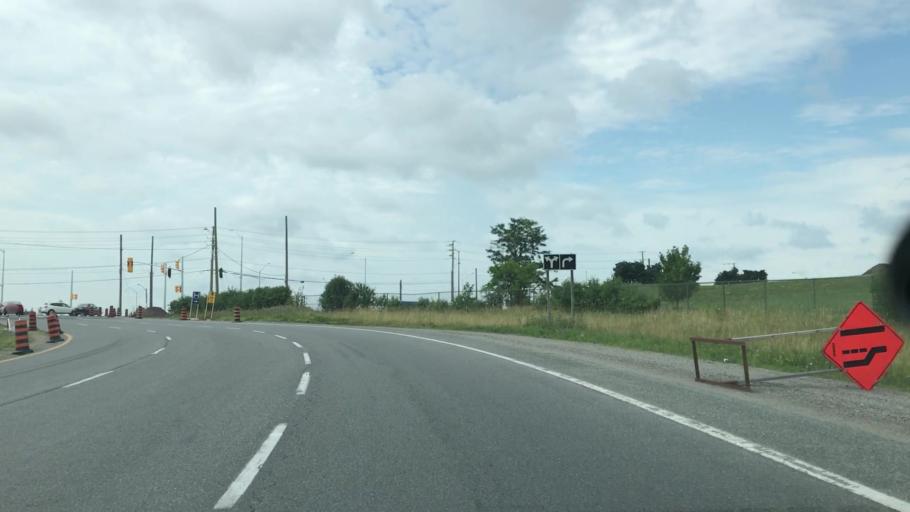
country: CA
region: Ontario
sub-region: York
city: Richmond Hill
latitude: 43.8839
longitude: -79.3820
